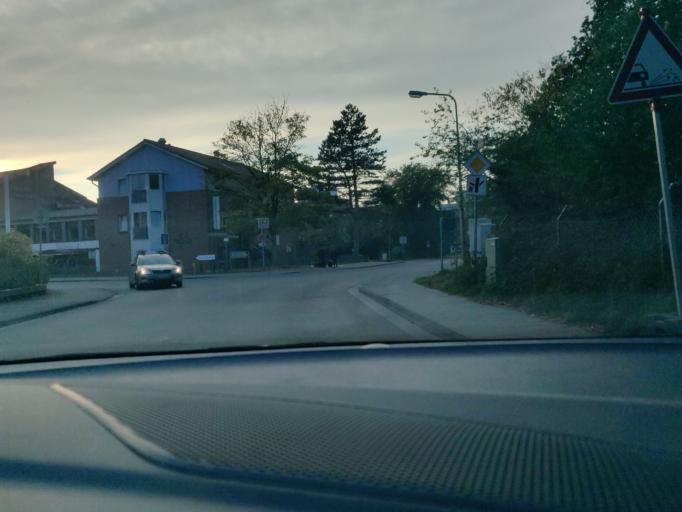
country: DE
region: Lower Saxony
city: Nordholz
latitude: 53.8614
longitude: 8.6048
